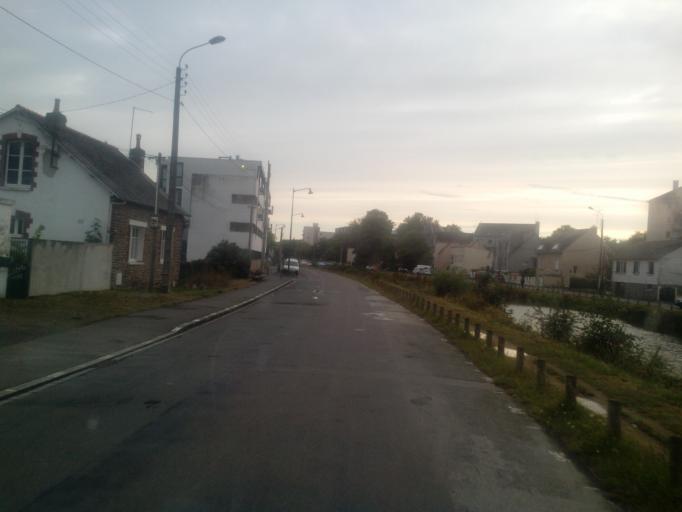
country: FR
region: Brittany
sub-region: Departement d'Ille-et-Vilaine
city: Rennes
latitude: 48.1230
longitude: -1.6784
